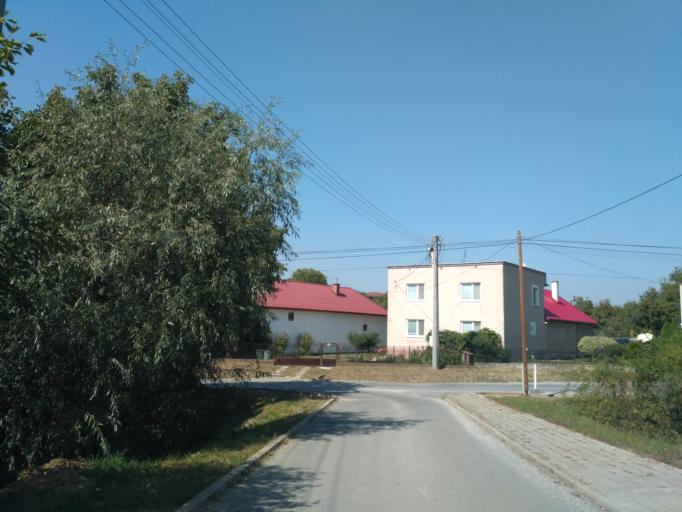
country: SK
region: Kosicky
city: Kosice
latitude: 48.7577
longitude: 21.3464
